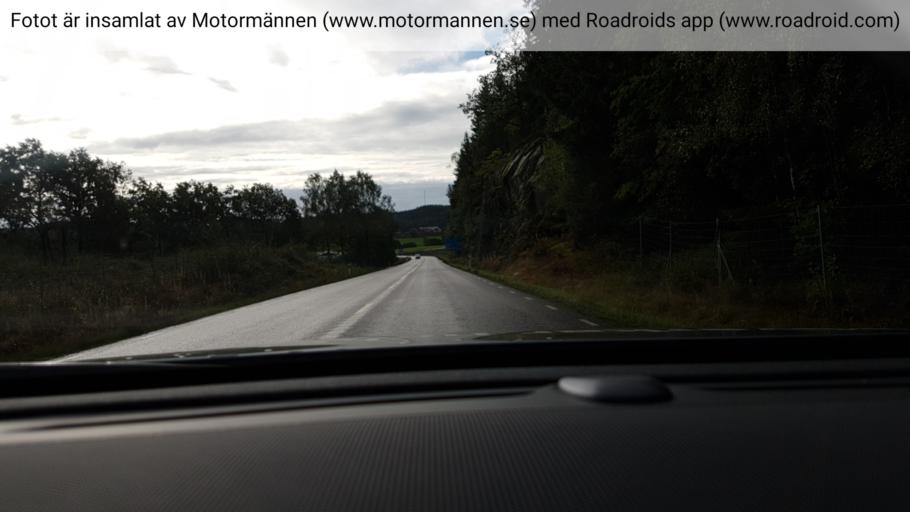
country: SE
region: Vaestra Goetaland
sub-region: Harryda Kommun
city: Ravlanda
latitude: 57.5589
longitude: 12.5176
